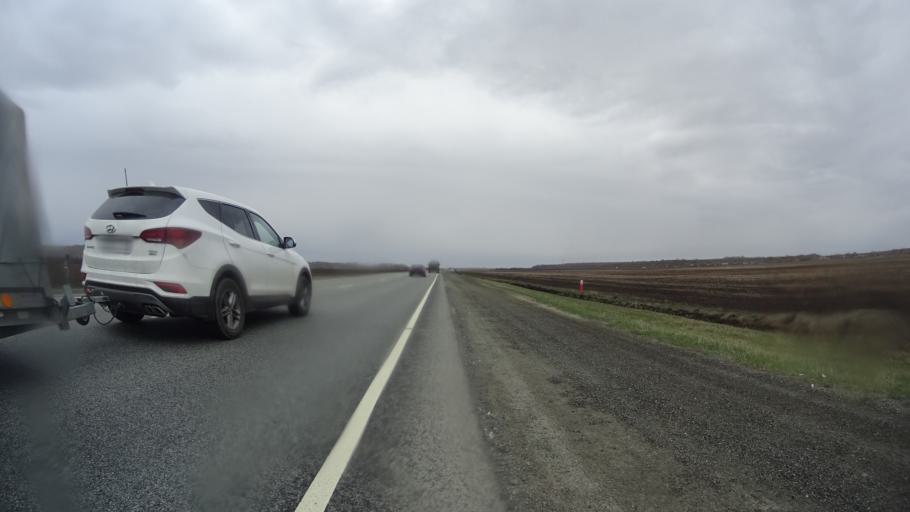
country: RU
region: Chelyabinsk
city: Krasnogorskiy
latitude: 54.5857
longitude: 61.2908
